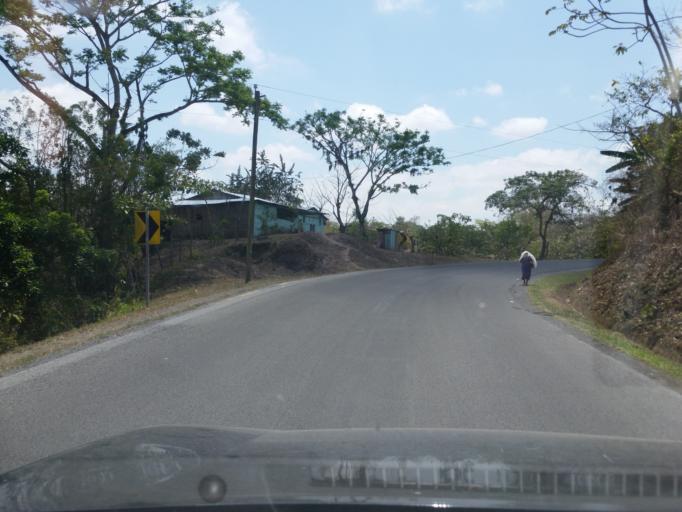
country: NI
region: Matagalpa
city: Muy Muy
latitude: 12.6075
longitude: -85.5394
